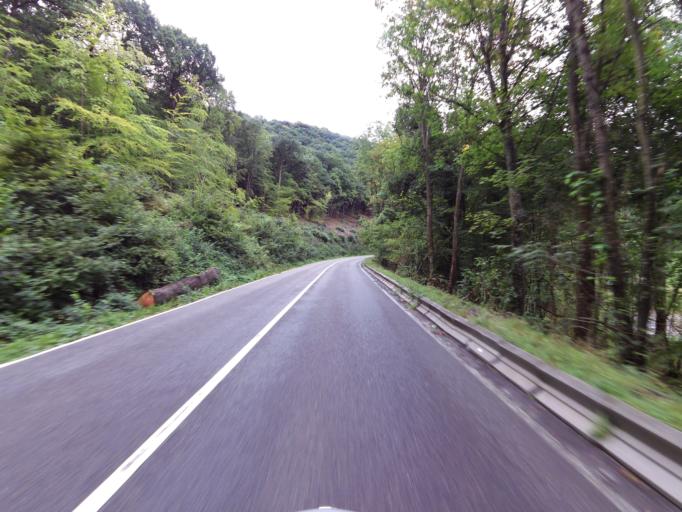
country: BE
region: Wallonia
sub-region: Province de Namur
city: Rochefort
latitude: 50.1431
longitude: 5.1946
